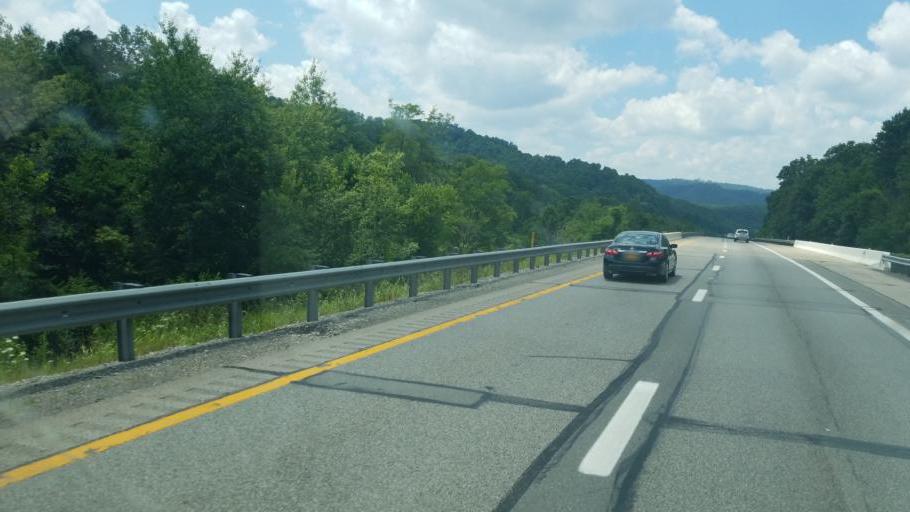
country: US
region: West Virginia
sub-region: Raleigh County
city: Prosperity
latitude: 37.8462
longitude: -81.2382
